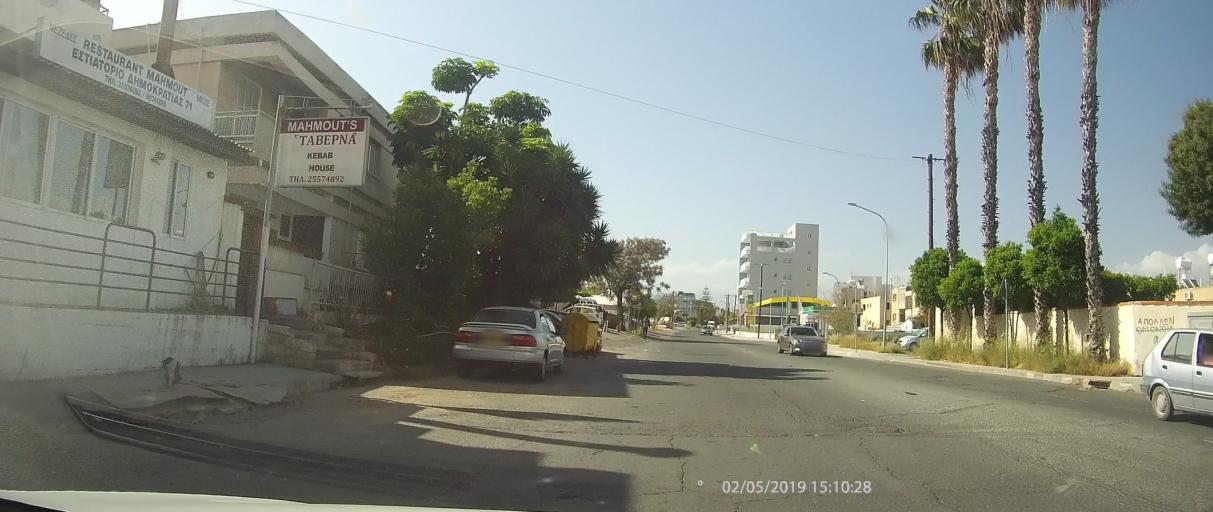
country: CY
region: Limassol
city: Limassol
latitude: 34.6681
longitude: 33.0243
